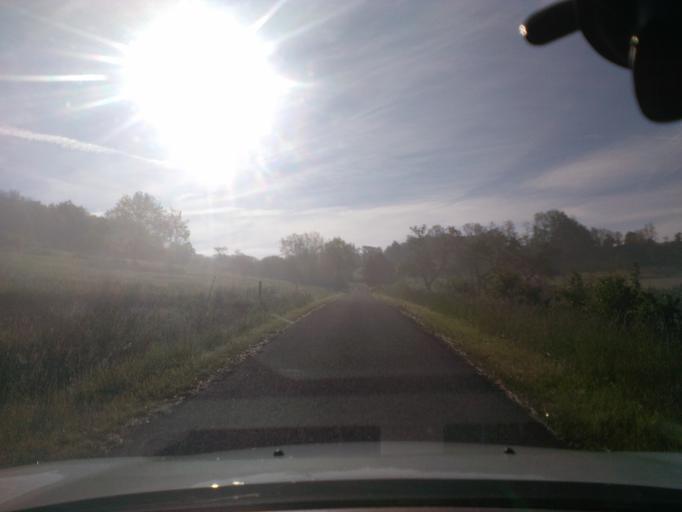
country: FR
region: Lorraine
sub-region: Departement des Vosges
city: Charmes
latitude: 48.3341
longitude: 6.2430
